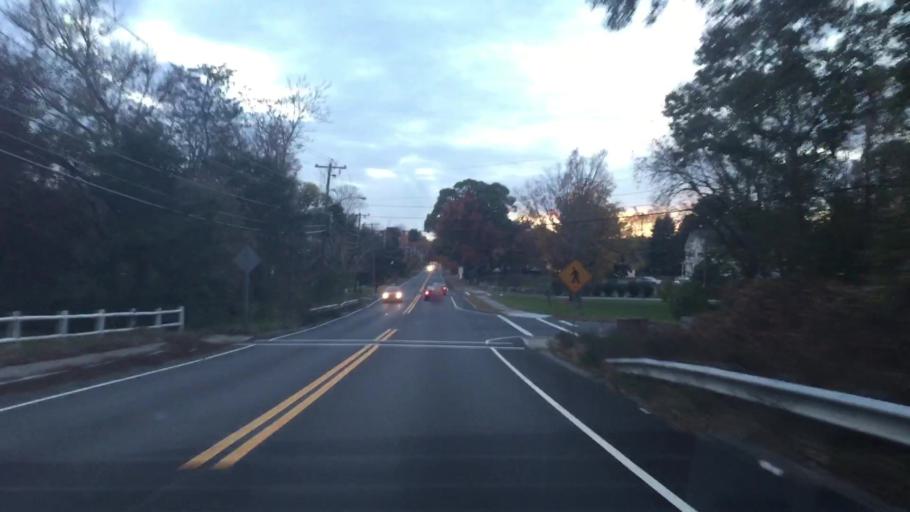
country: US
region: Massachusetts
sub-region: Middlesex County
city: Tewksbury
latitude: 42.6439
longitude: -71.2577
